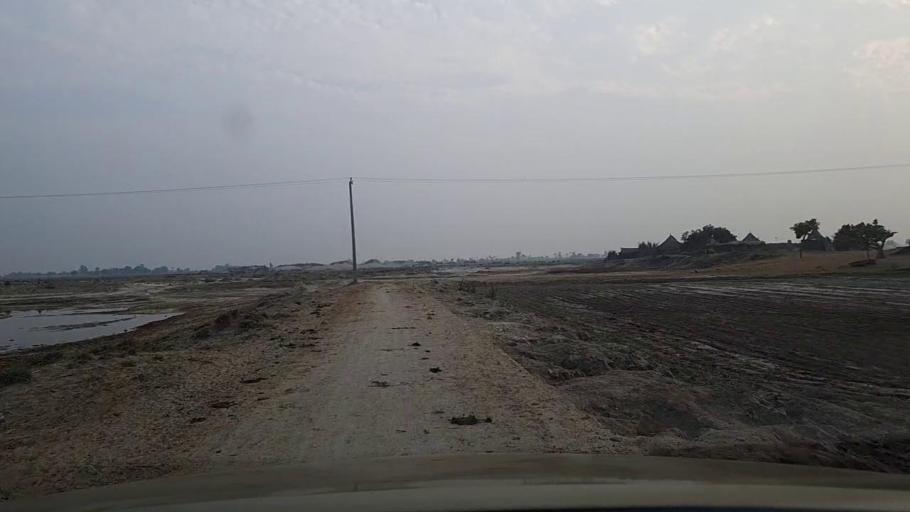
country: PK
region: Sindh
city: Sanghar
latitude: 26.2303
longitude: 68.9427
